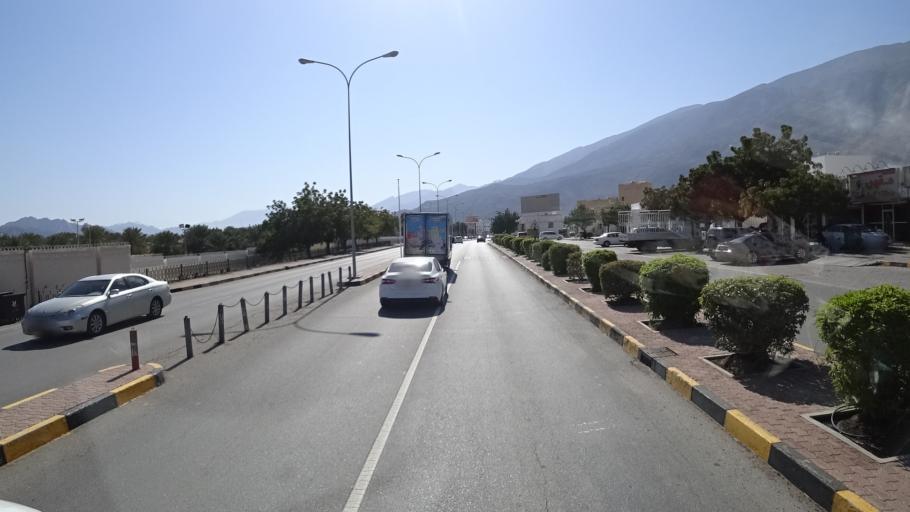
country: OM
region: Al Batinah
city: Rustaq
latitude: 23.3978
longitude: 57.4211
